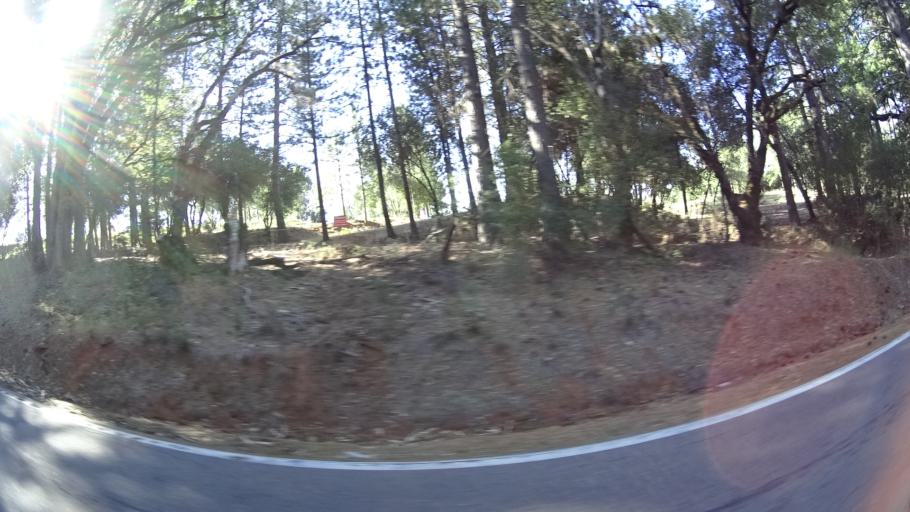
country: US
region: California
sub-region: Amador County
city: Pioneer
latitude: 38.3807
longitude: -120.5307
